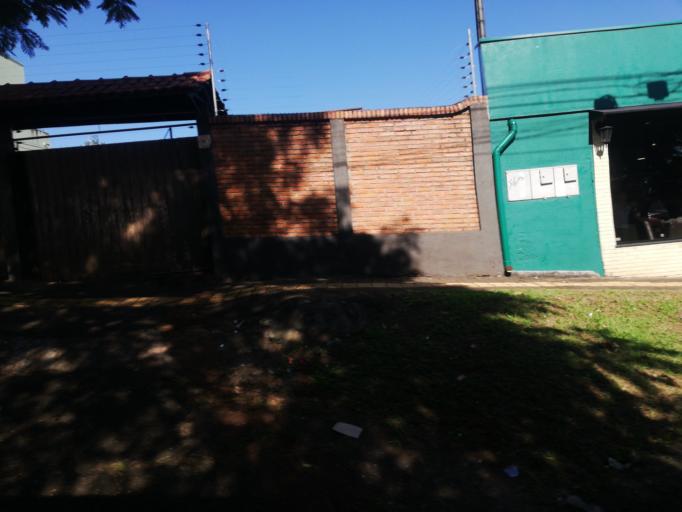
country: BR
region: Parana
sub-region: Foz Do Iguacu
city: Foz do Iguacu
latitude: -25.5502
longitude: -54.5738
